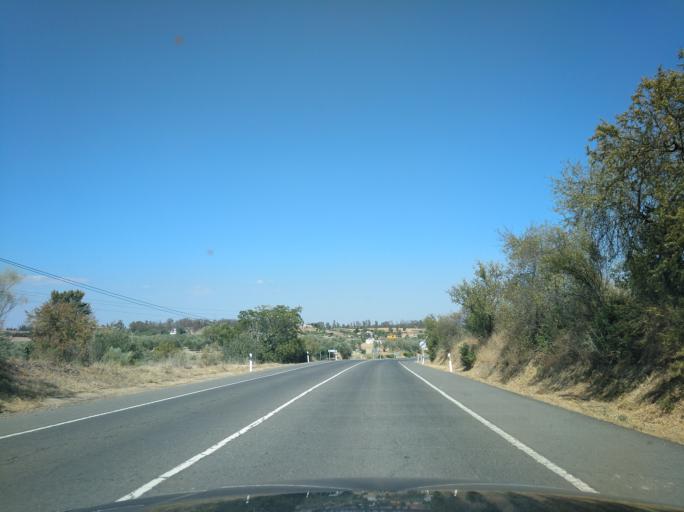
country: ES
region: Andalusia
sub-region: Provincia de Huelva
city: Gibraleon
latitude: 37.3539
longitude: -7.0090
